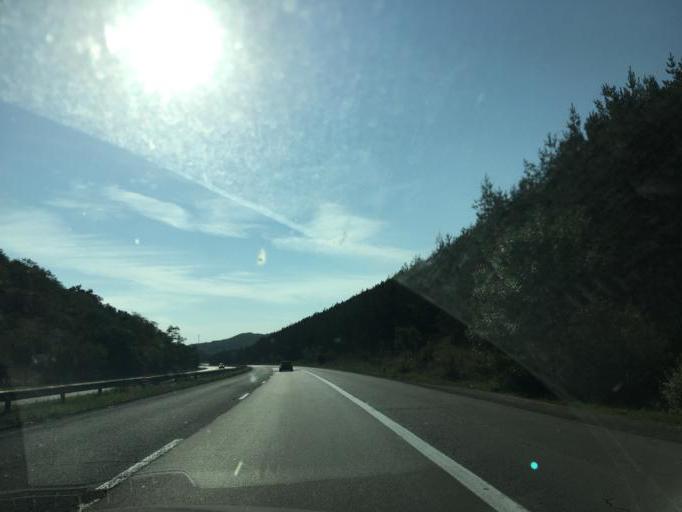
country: BG
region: Sofiya
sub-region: Obshtina Ikhtiman
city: Ikhtiman
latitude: 42.3655
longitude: 23.8948
